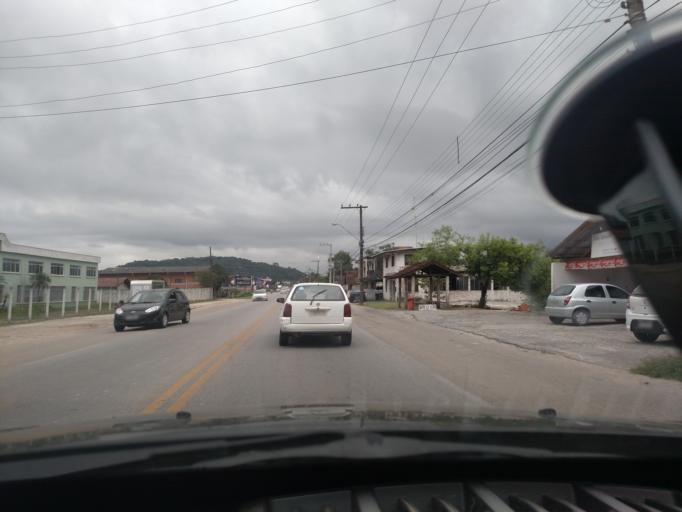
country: BR
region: Santa Catarina
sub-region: Gaspar
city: Gaspar
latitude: -26.9160
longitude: -48.9783
